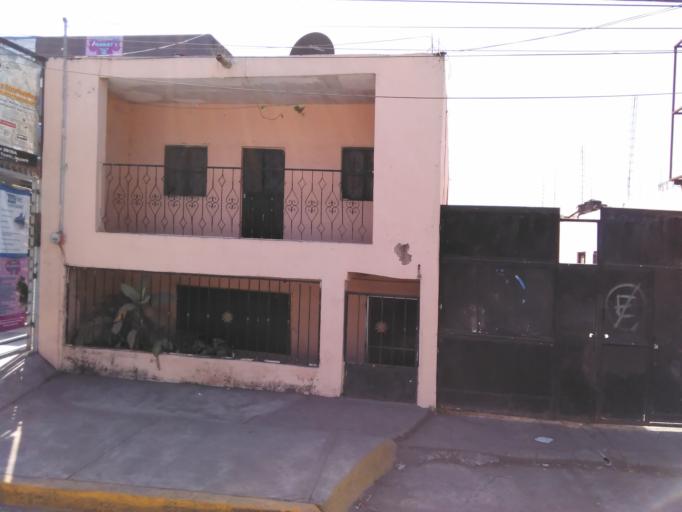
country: MX
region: Nayarit
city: Xalisco
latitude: 21.4733
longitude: -104.8569
